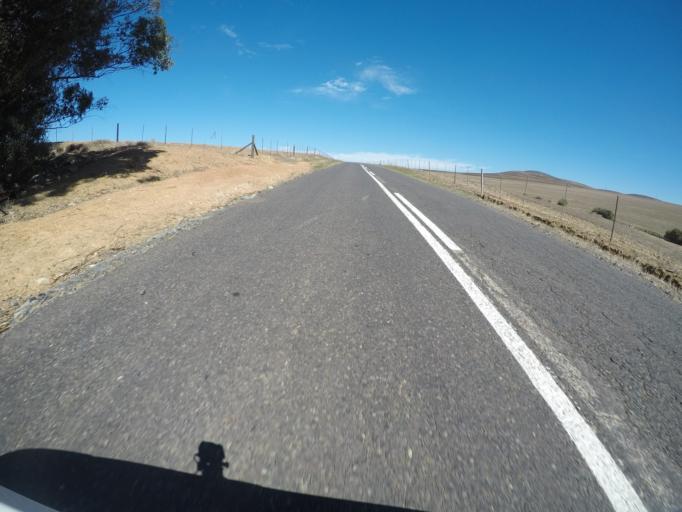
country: ZA
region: Western Cape
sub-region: City of Cape Town
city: Atlantis
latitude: -33.7004
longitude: 18.5883
